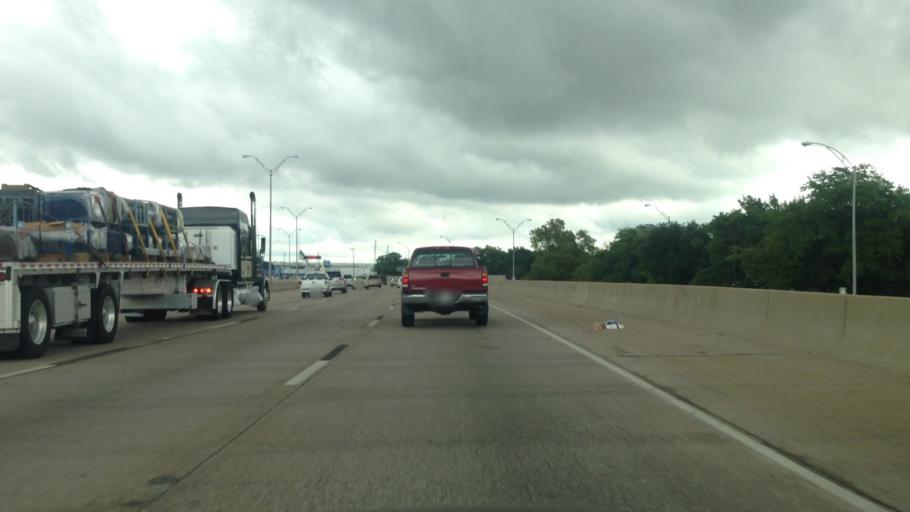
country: US
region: Texas
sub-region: Tarrant County
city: Edgecliff Village
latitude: 32.6636
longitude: -97.3403
